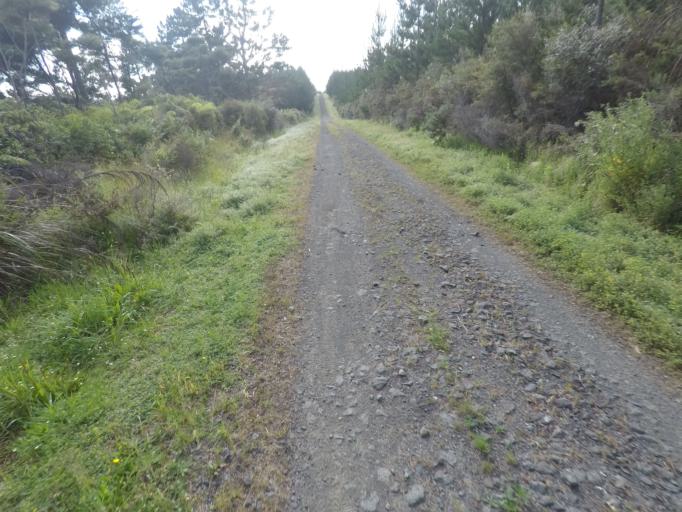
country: NZ
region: Auckland
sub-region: Auckland
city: Rothesay Bay
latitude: -36.7093
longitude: 174.5831
